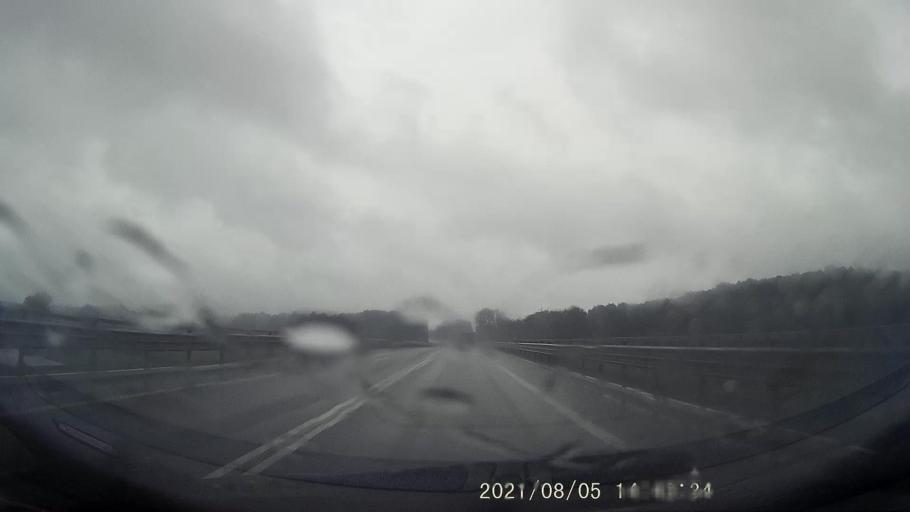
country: PL
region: Opole Voivodeship
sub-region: Powiat nyski
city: Nysa
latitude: 50.4850
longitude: 17.3886
